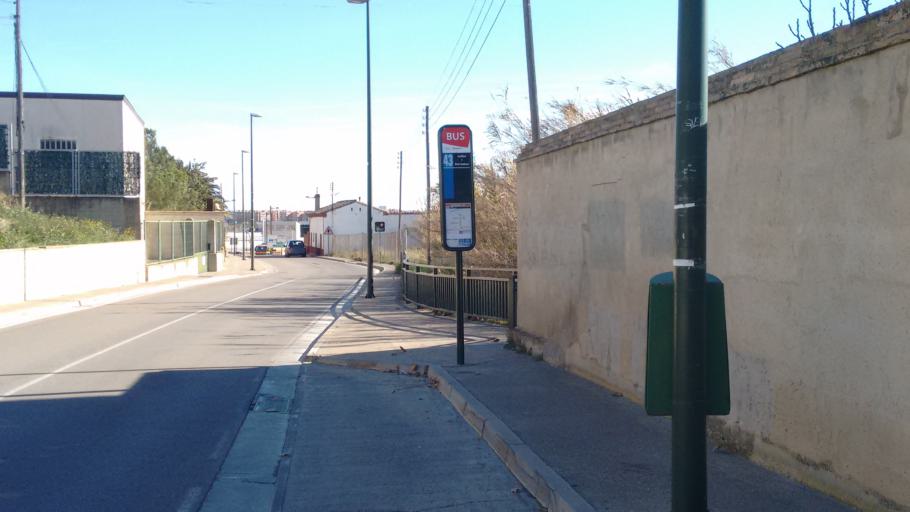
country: ES
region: Aragon
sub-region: Provincia de Zaragoza
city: Almozara
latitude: 41.6884
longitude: -0.8916
